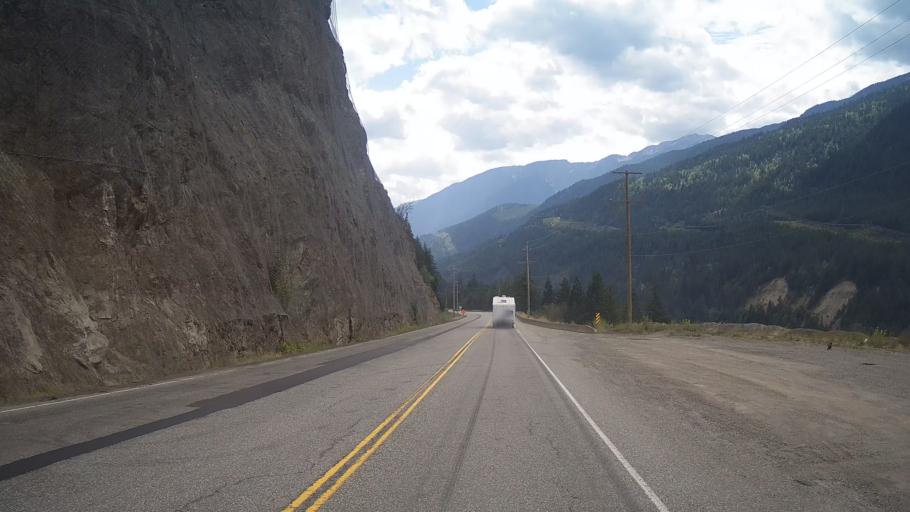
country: CA
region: British Columbia
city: Hope
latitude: 50.0653
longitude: -121.5448
